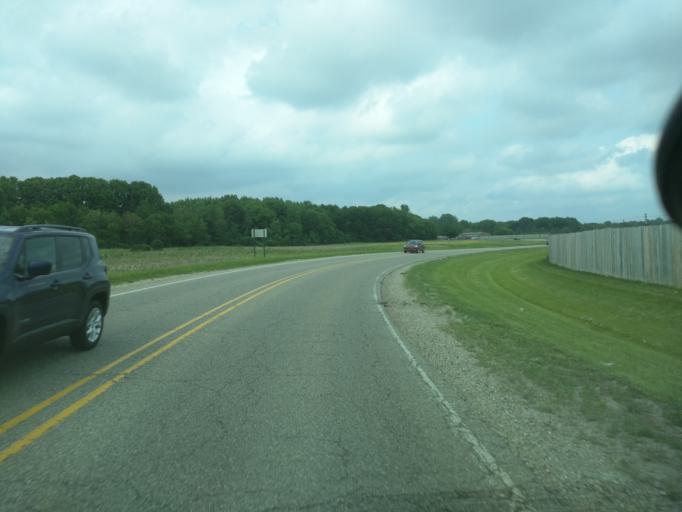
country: US
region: Michigan
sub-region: Ingham County
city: Edgemont Park
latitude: 42.7785
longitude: -84.6069
